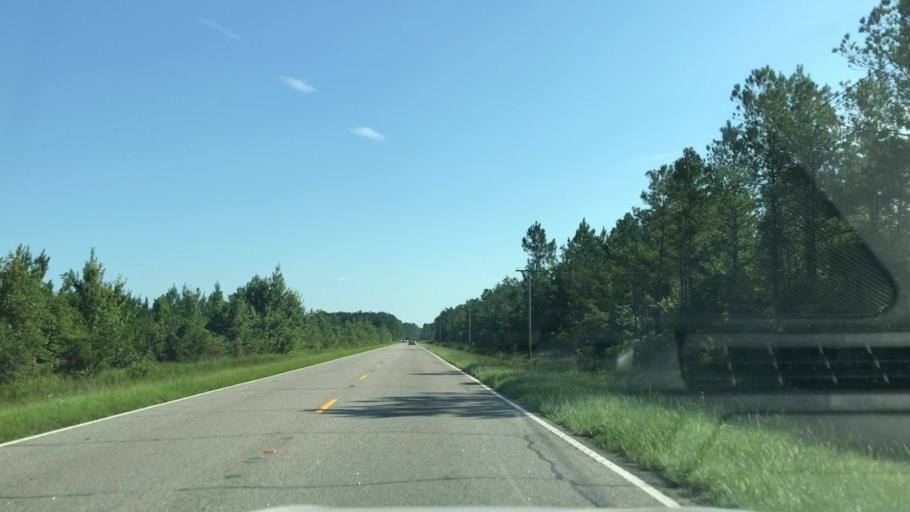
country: US
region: South Carolina
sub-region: Georgetown County
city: Georgetown
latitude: 33.5151
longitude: -79.2492
